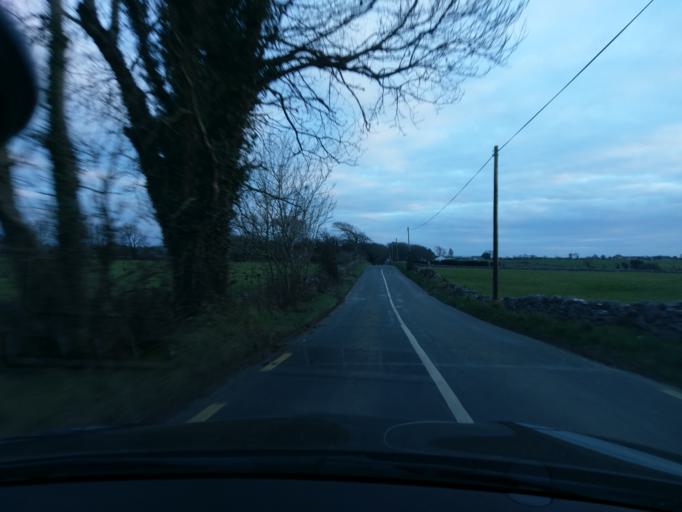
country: IE
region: Connaught
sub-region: County Galway
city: Athenry
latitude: 53.3422
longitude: -8.7753
